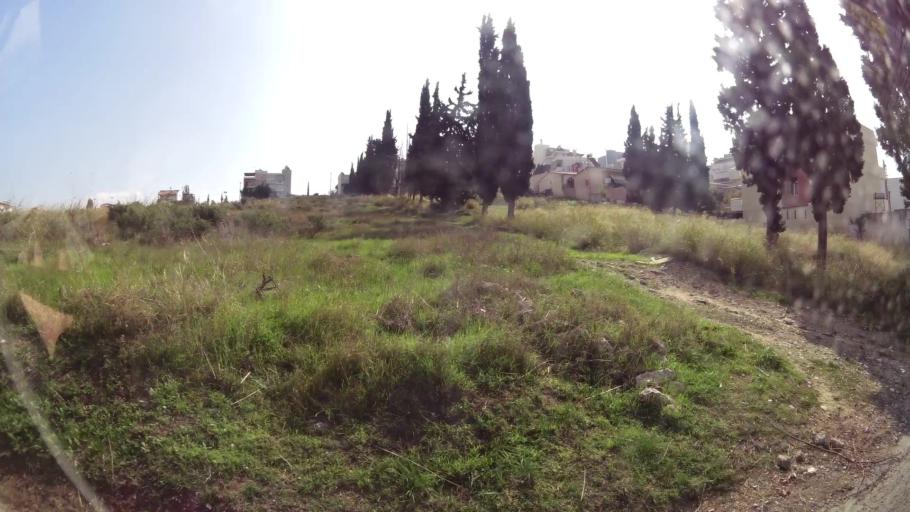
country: GR
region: Attica
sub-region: Nomarchia Dytikis Attikis
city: Zefyri
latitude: 38.0626
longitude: 23.7225
